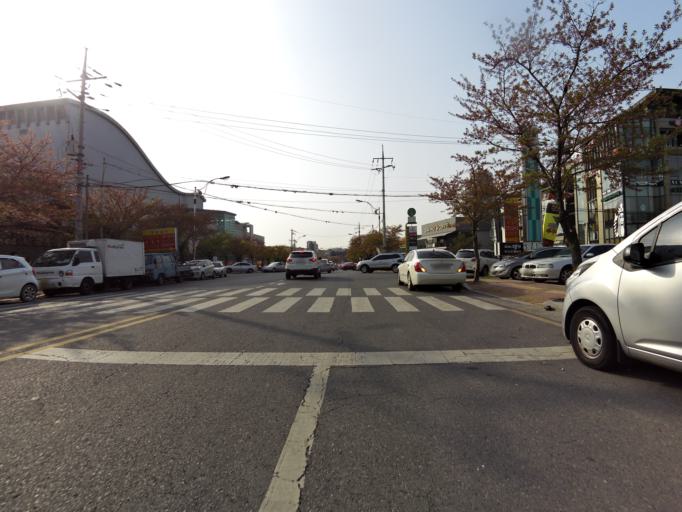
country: KR
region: Daegu
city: Daegu
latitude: 35.8794
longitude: 128.6535
